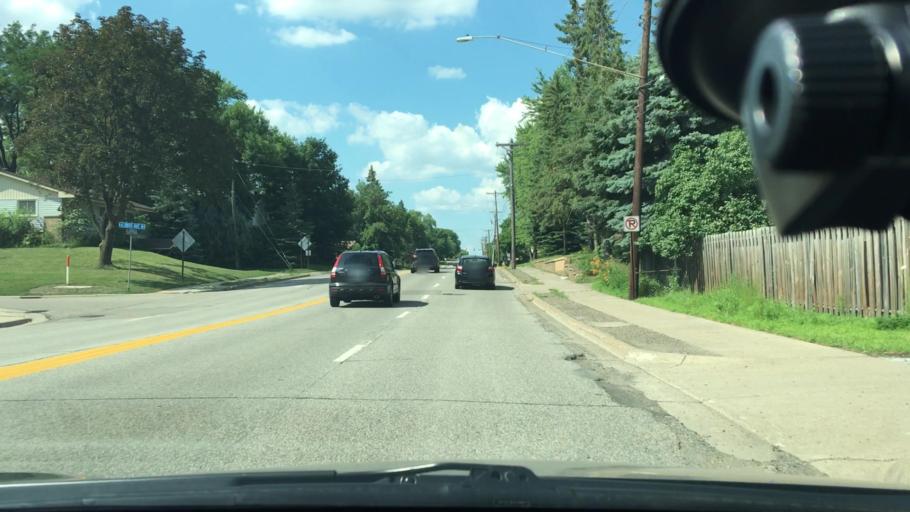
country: US
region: Minnesota
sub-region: Hennepin County
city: New Hope
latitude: 45.0095
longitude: -93.3802
